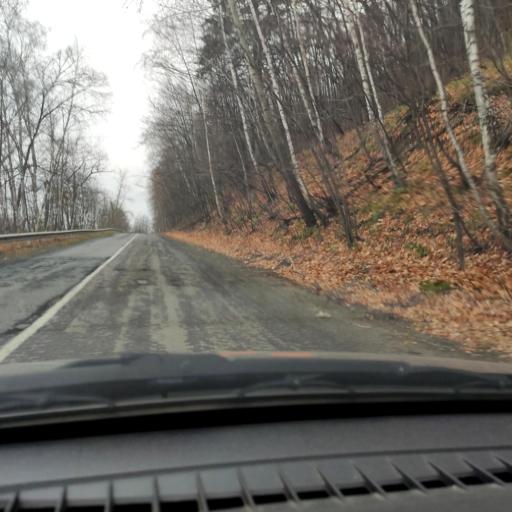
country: RU
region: Samara
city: Povolzhskiy
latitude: 53.4381
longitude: 49.6800
